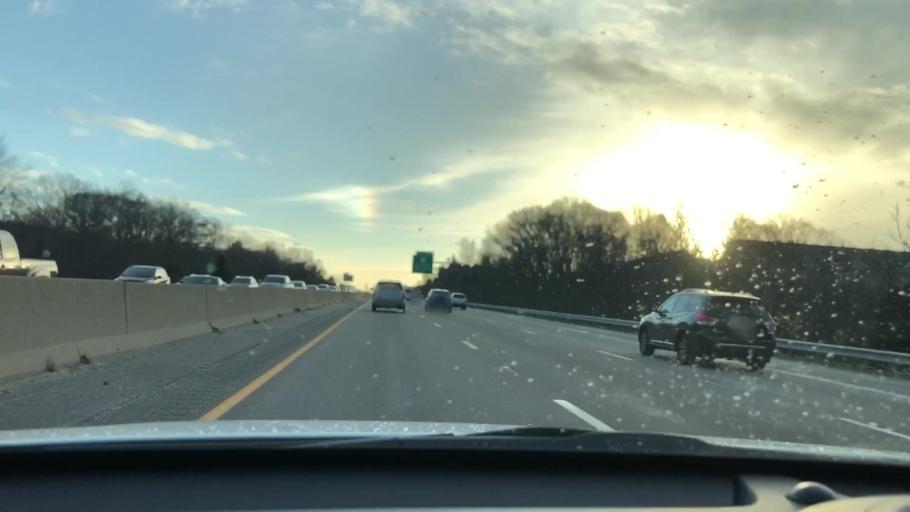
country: US
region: Massachusetts
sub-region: Norfolk County
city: Braintree
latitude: 42.2016
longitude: -70.9785
